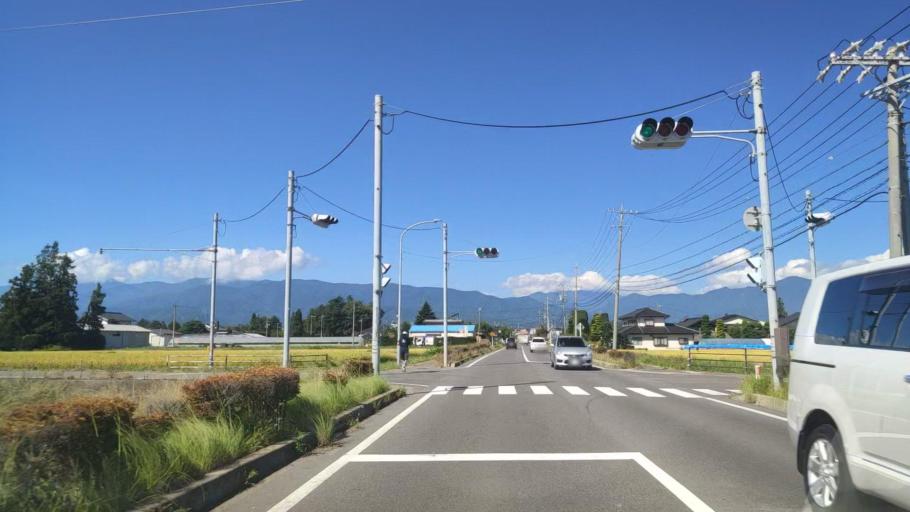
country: JP
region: Nagano
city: Shiojiri
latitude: 36.1646
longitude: 137.9398
